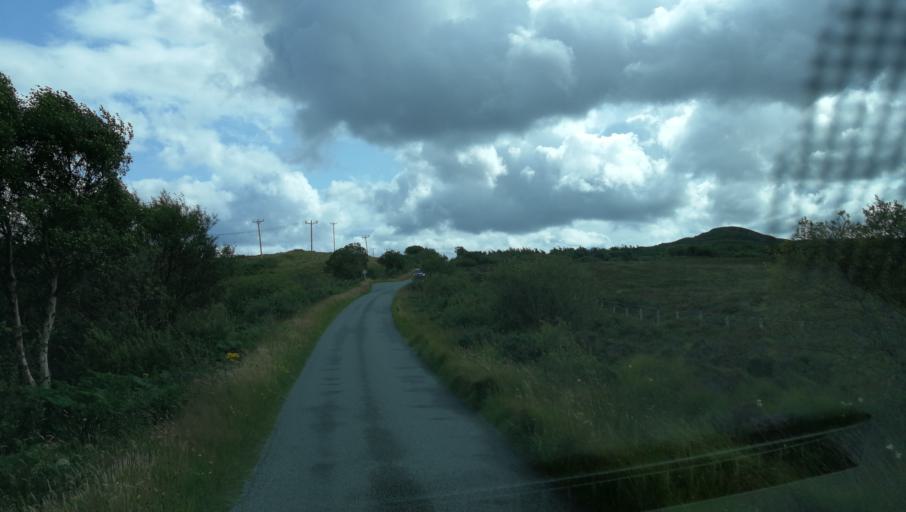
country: GB
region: Scotland
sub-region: Highland
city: Portree
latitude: 57.3823
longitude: -6.1749
